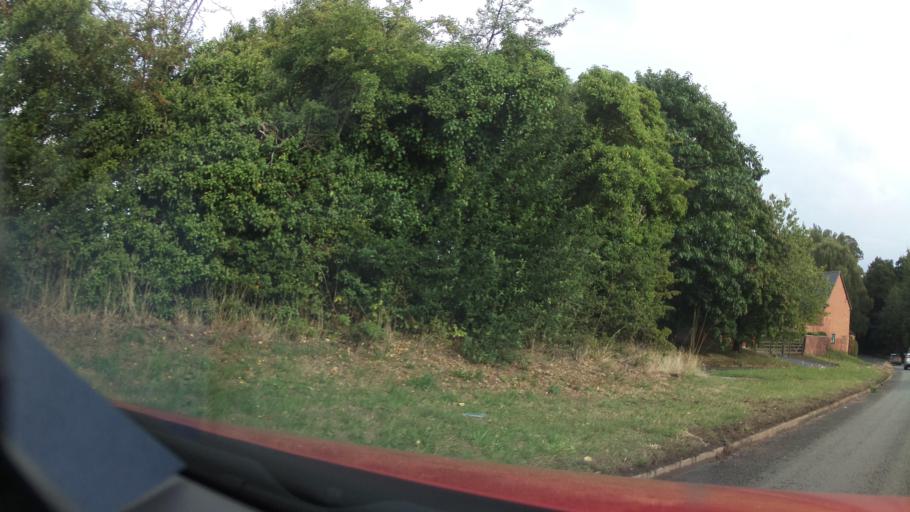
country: GB
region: England
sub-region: Worcestershire
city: Kidderminster
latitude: 52.3771
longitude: -2.2257
